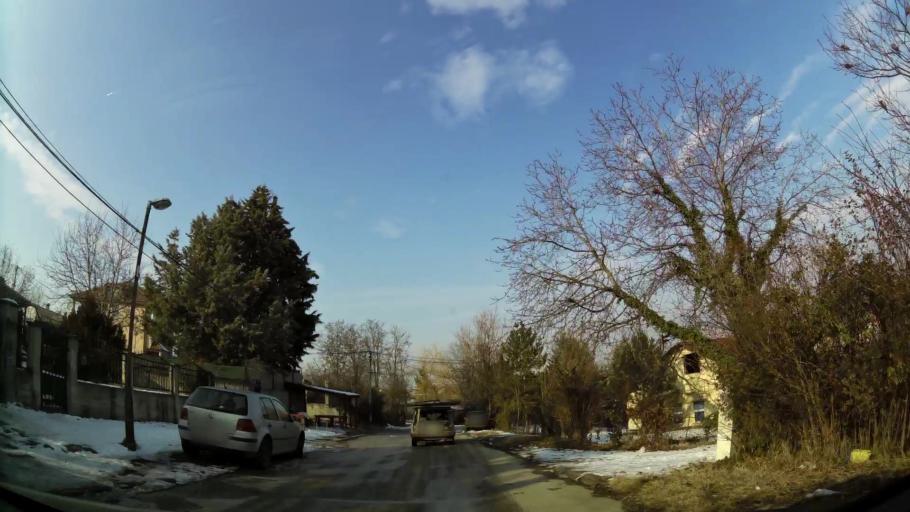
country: MK
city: Creshevo
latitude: 42.0157
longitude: 21.5052
